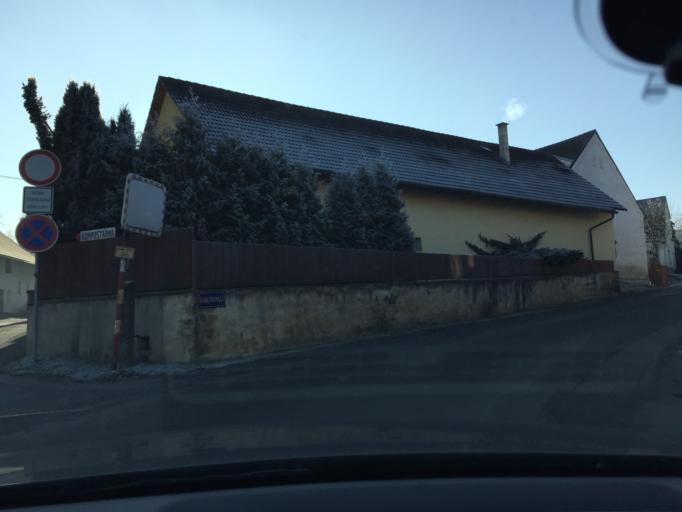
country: CZ
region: Central Bohemia
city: Trebotov
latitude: 49.9944
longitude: 14.2644
